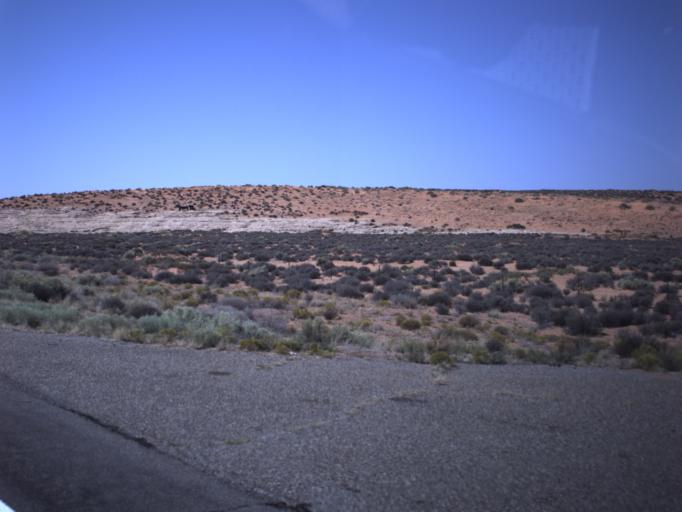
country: US
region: Utah
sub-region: San Juan County
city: Blanding
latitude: 37.0648
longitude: -109.5580
